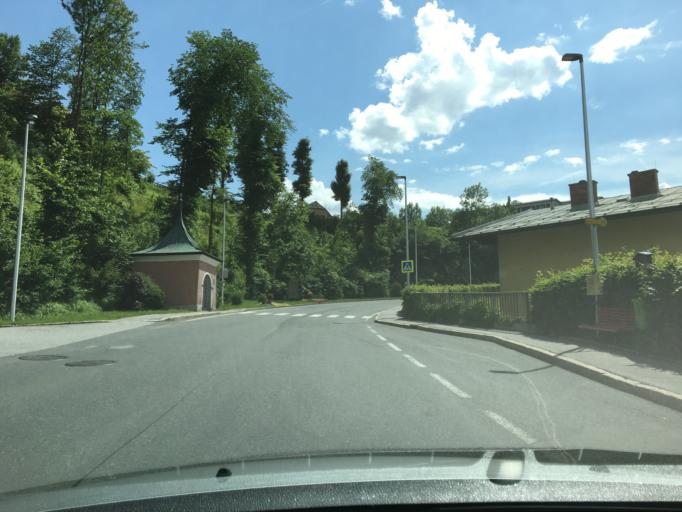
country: AT
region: Salzburg
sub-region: Politischer Bezirk Sankt Johann im Pongau
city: Sankt Johann im Pongau
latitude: 47.3527
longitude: 13.2069
